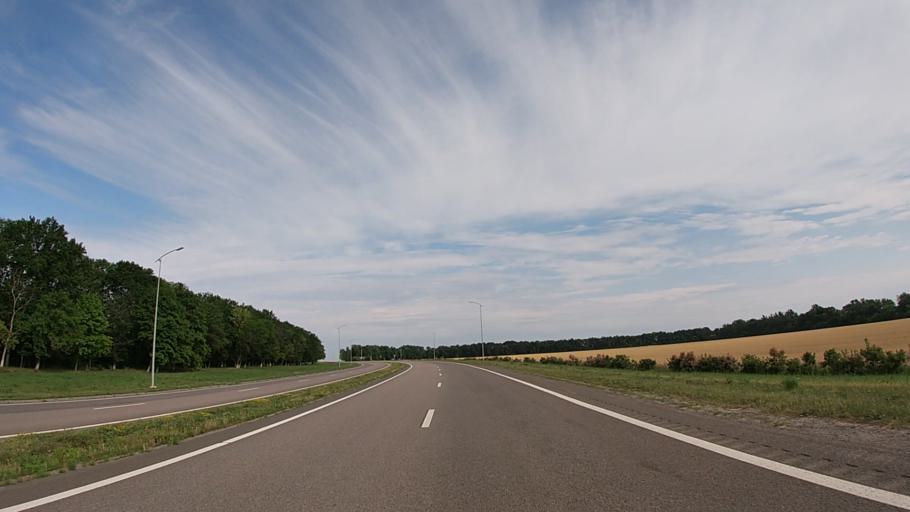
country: RU
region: Belgorod
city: Rakitnoye
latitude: 50.7605
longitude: 35.9630
